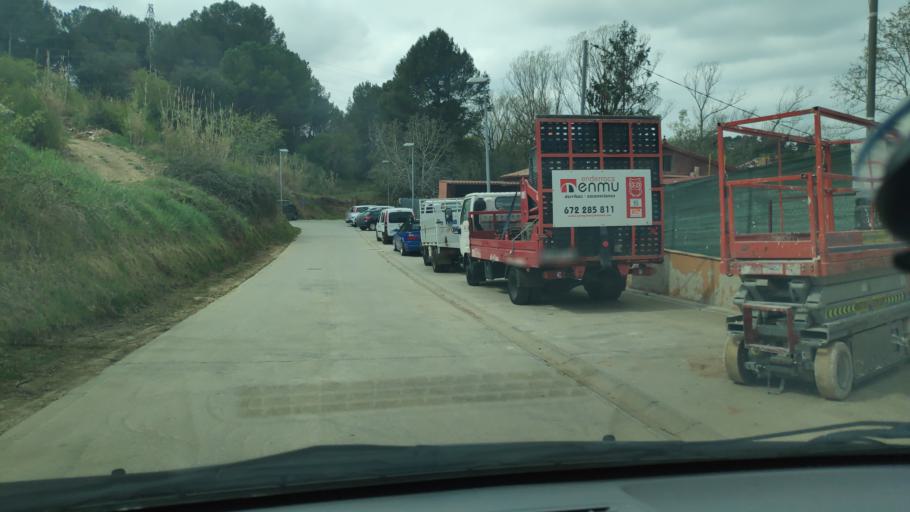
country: ES
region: Catalonia
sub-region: Provincia de Barcelona
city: Sant Quirze del Valles
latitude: 41.5222
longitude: 2.0865
